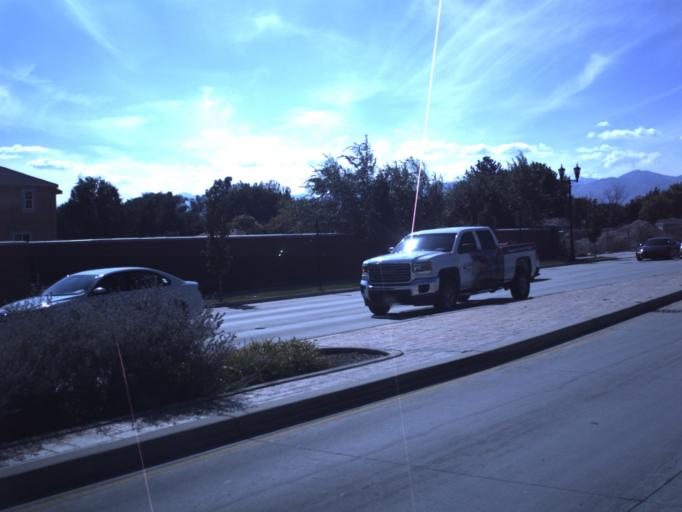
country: US
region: Utah
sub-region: Salt Lake County
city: South Jordan Heights
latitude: 40.5623
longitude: -111.9467
